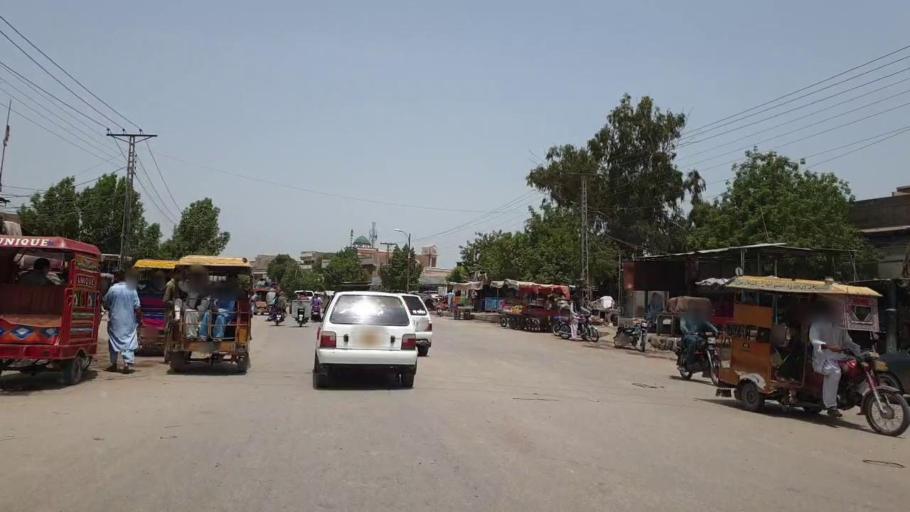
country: PK
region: Sindh
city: Nawabshah
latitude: 26.2518
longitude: 68.4251
